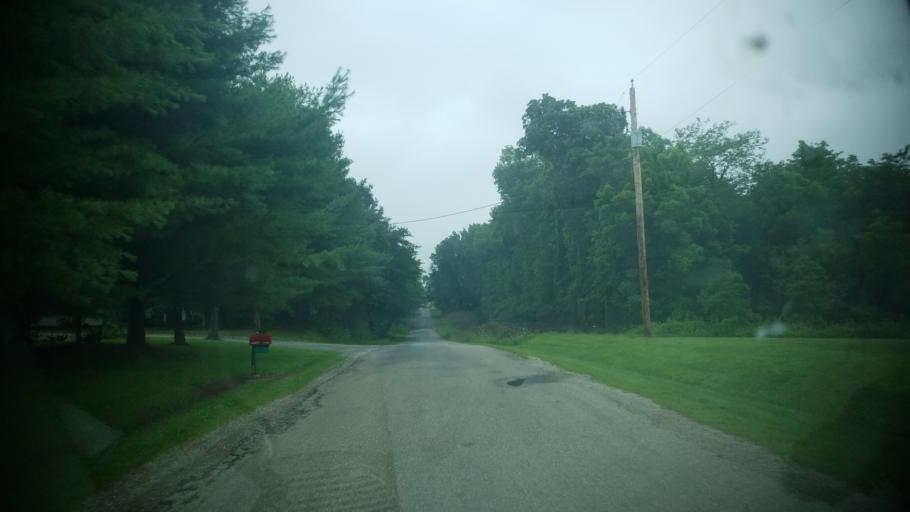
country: US
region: Illinois
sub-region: Clay County
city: Flora
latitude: 38.6694
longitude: -88.3548
